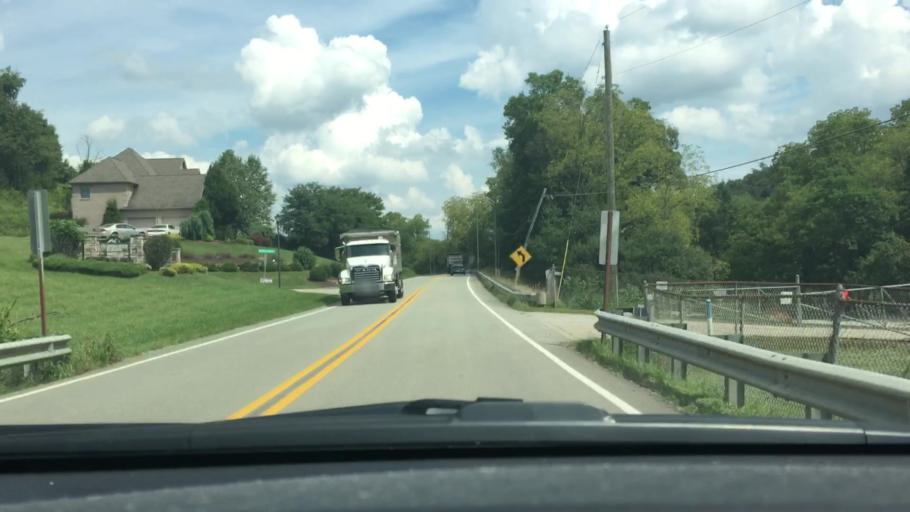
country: US
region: Pennsylvania
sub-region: Washington County
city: McMurray
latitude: 40.2384
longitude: -80.0761
